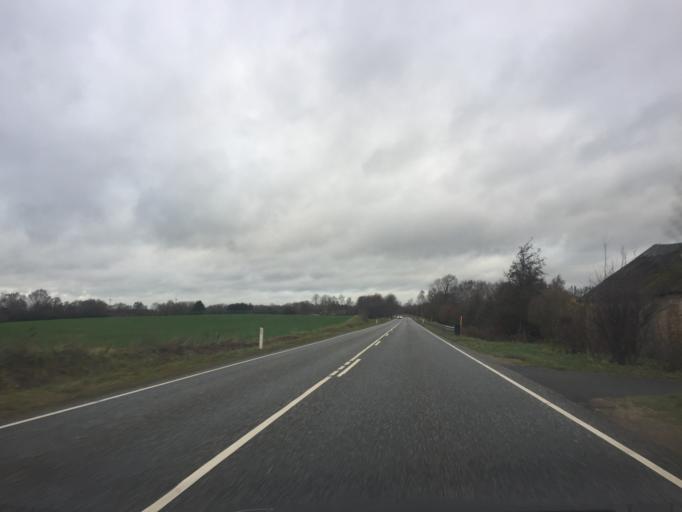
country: DK
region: Zealand
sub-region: Soro Kommune
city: Stenlille
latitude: 55.4994
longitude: 11.5802
